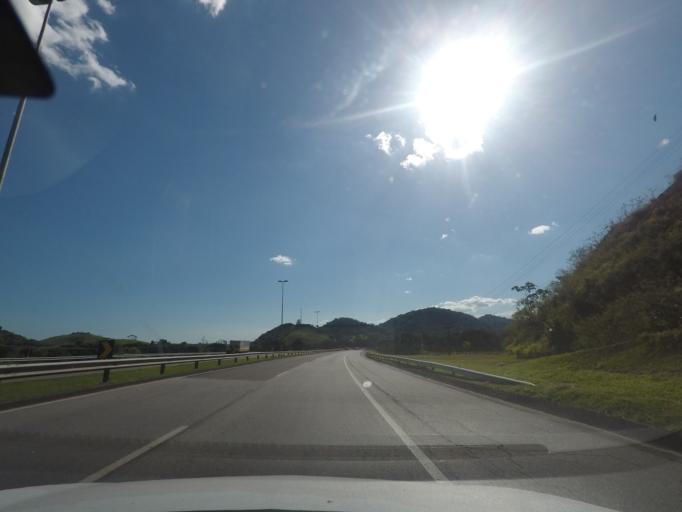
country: BR
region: Rio de Janeiro
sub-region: Guapimirim
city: Guapimirim
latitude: -22.6149
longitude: -43.0364
